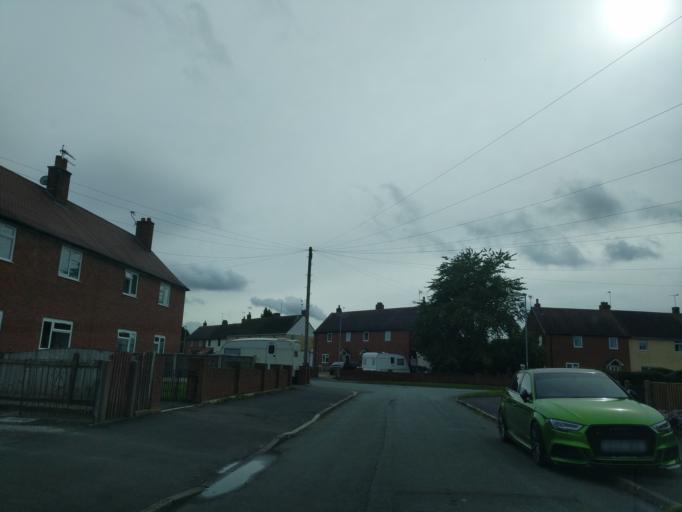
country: GB
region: England
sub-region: Staffordshire
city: Audley
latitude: 52.9978
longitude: -2.3424
